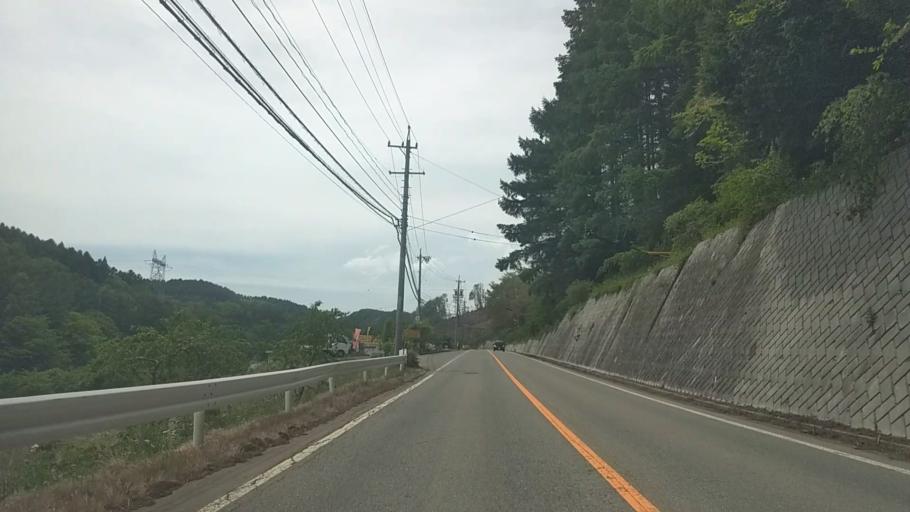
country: JP
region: Nagano
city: Saku
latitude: 36.1232
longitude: 138.4532
